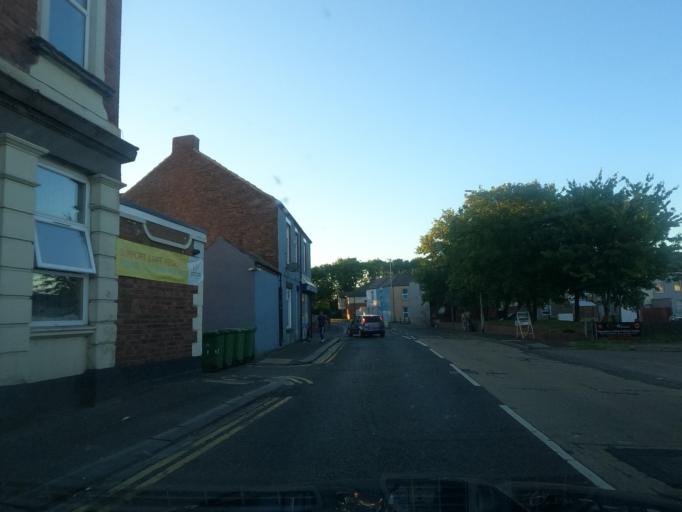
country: GB
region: England
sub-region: Northumberland
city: Blyth
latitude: 55.1263
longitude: -1.5170
